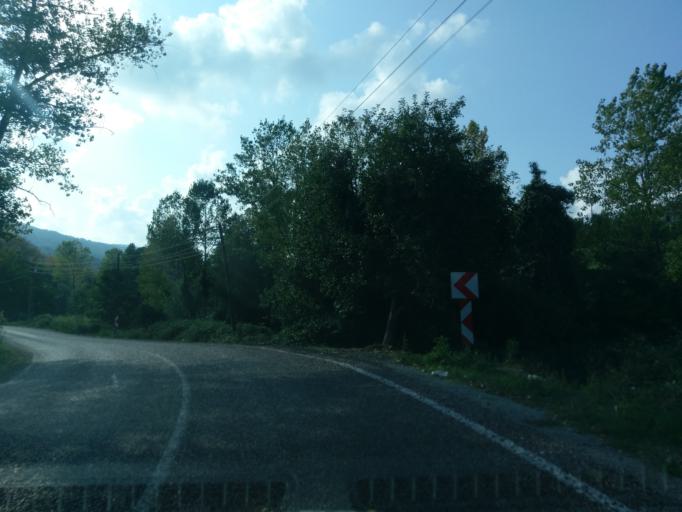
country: TR
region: Sinop
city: Helaldi
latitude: 41.8909
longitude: 34.4885
